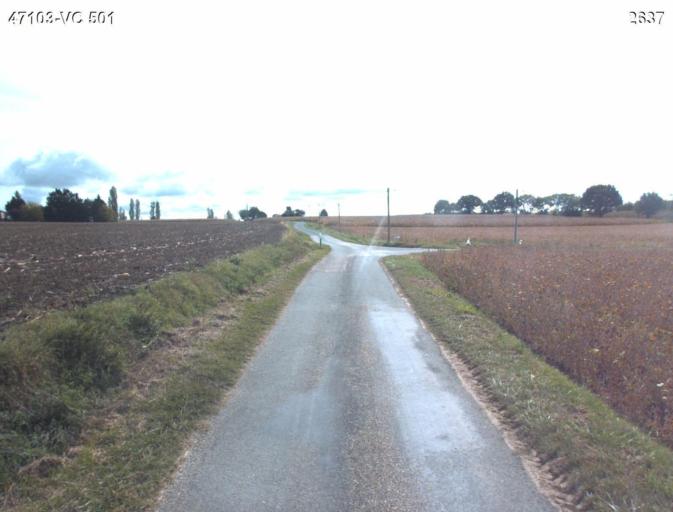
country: FR
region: Aquitaine
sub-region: Departement du Lot-et-Garonne
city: Nerac
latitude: 44.0990
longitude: 0.3235
